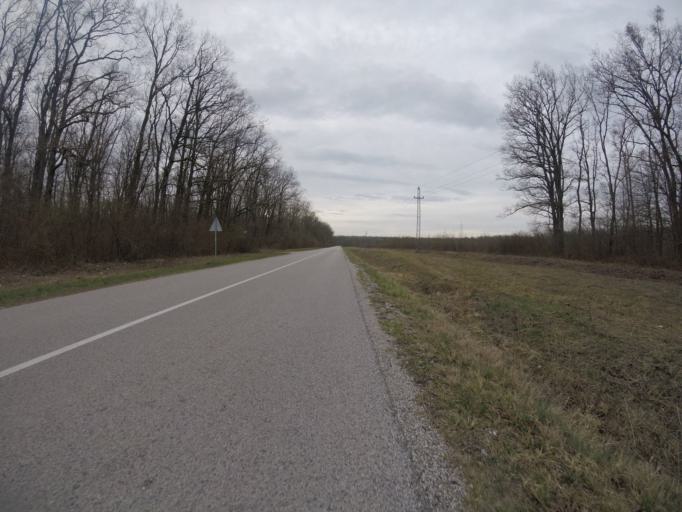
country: HR
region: Zagrebacka
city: Lukavec
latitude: 45.6884
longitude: 15.9807
